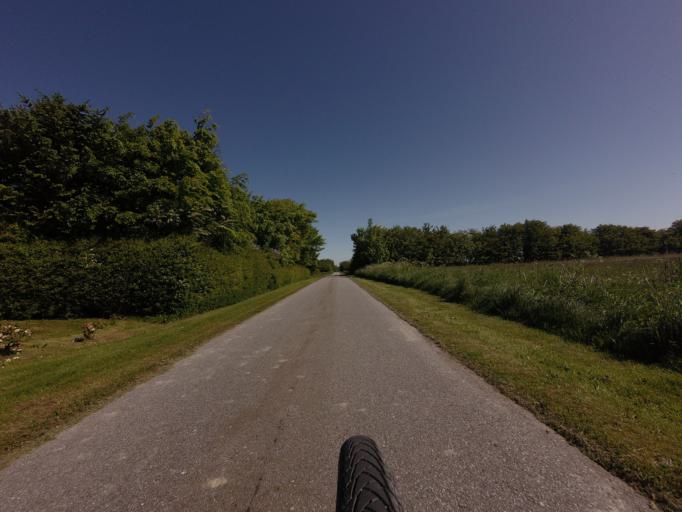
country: DK
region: North Denmark
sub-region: Hjorring Kommune
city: Vra
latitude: 57.3782
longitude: 9.8155
